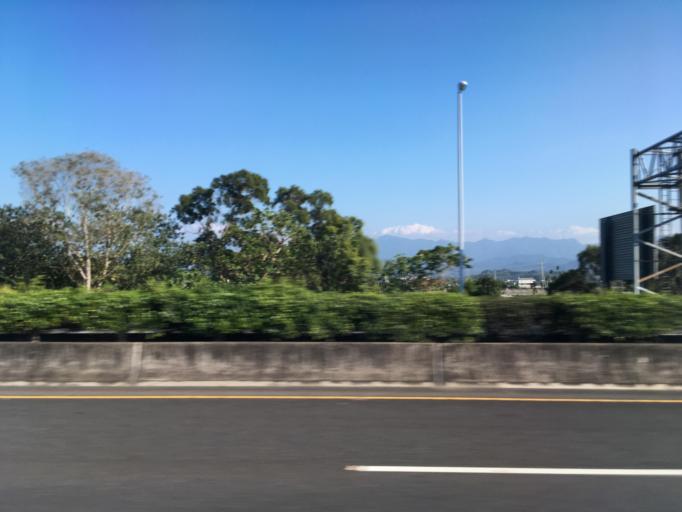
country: TW
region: Taiwan
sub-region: Chiayi
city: Jiayi Shi
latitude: 23.4452
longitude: 120.4822
